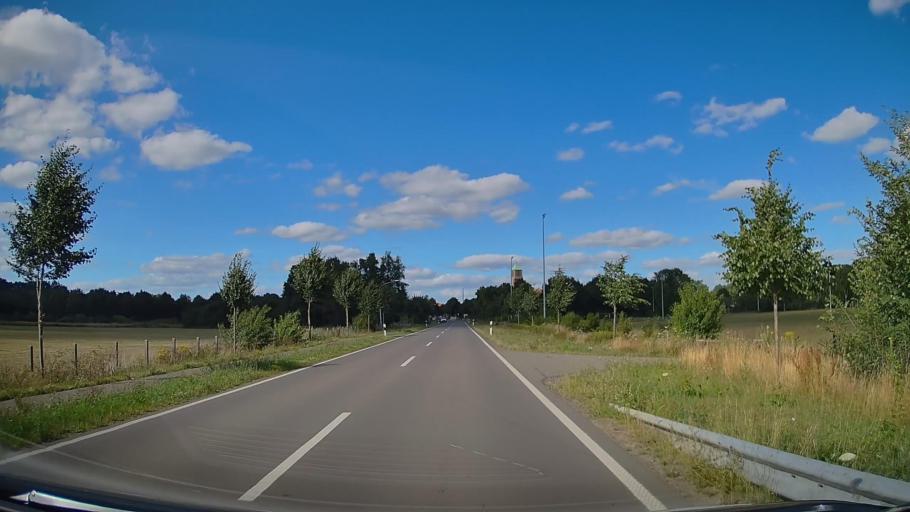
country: DE
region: Lower Saxony
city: Loningen
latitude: 52.7287
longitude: 7.7537
